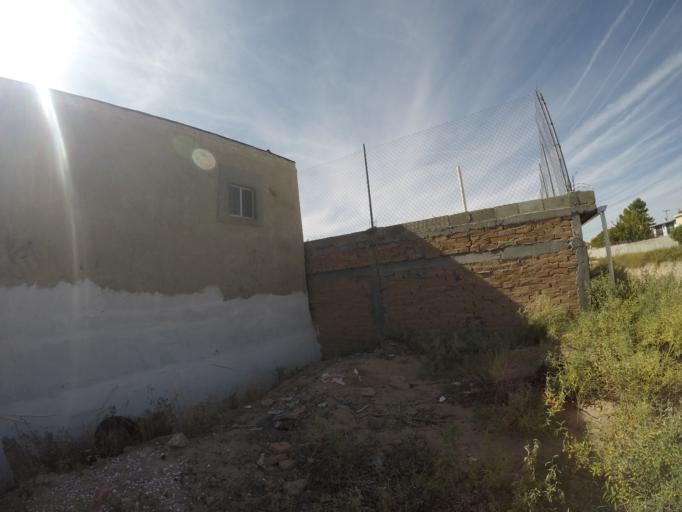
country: MX
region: Chihuahua
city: Ciudad Juarez
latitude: 31.7350
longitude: -106.4367
